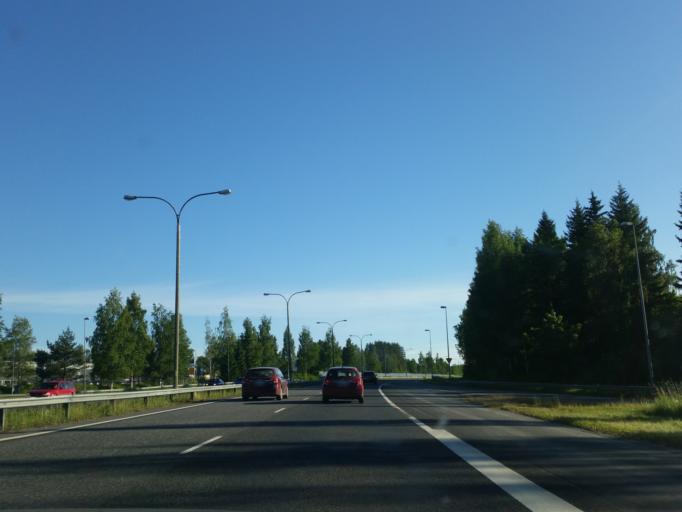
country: FI
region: Northern Savo
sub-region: Kuopio
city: Kuopio
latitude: 62.8820
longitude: 27.6335
